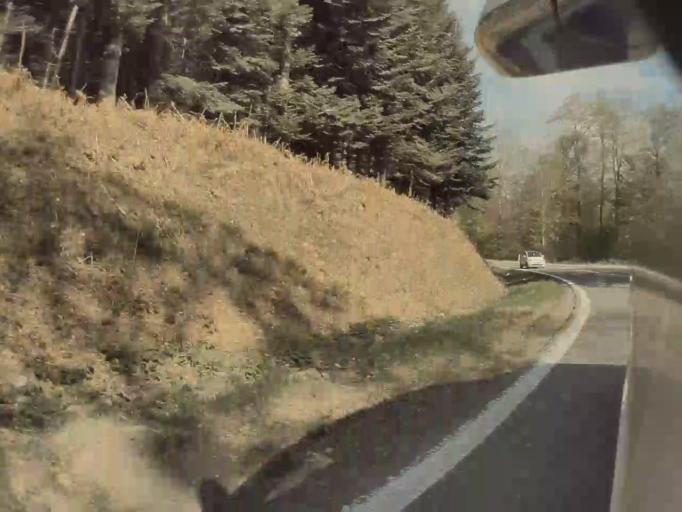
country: BE
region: Wallonia
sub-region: Province du Luxembourg
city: Tellin
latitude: 50.0190
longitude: 5.2056
